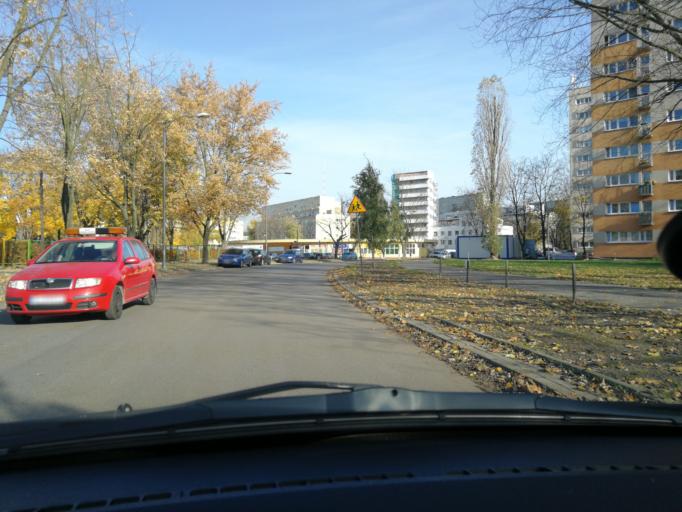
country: PL
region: Masovian Voivodeship
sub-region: Warszawa
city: Bielany
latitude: 52.2952
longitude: 20.9388
